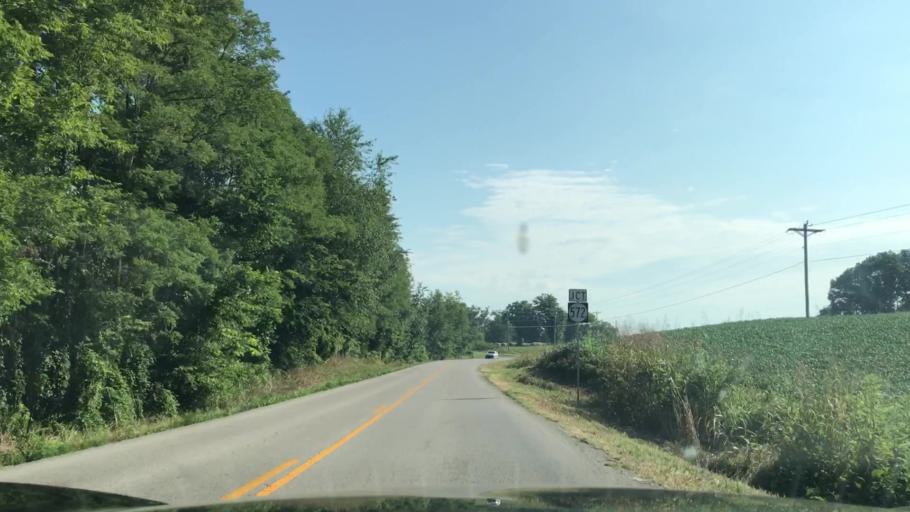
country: US
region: Kentucky
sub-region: Hart County
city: Horse Cave
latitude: 37.1738
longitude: -85.7921
